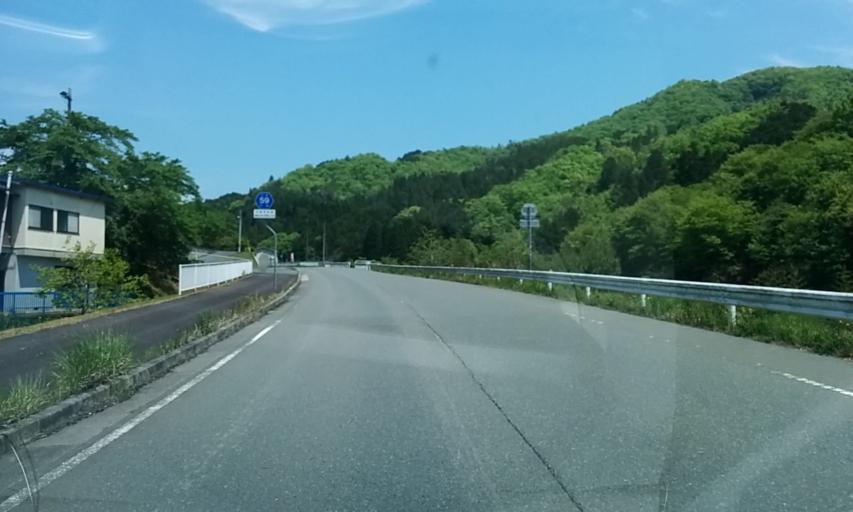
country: JP
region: Kyoto
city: Ayabe
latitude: 35.2433
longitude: 135.2639
